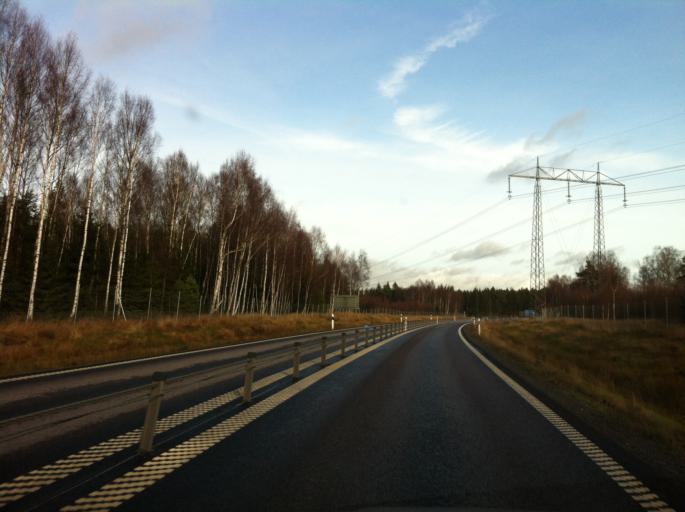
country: SE
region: Kronoberg
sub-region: Almhults Kommun
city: AElmhult
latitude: 56.6215
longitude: 14.2432
